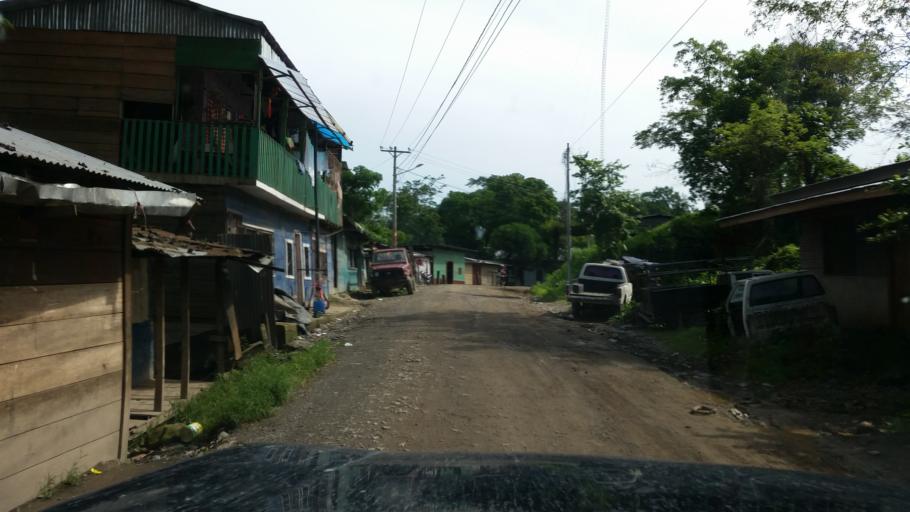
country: NI
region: Atlantico Norte (RAAN)
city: Siuna
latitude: 13.7175
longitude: -84.7674
